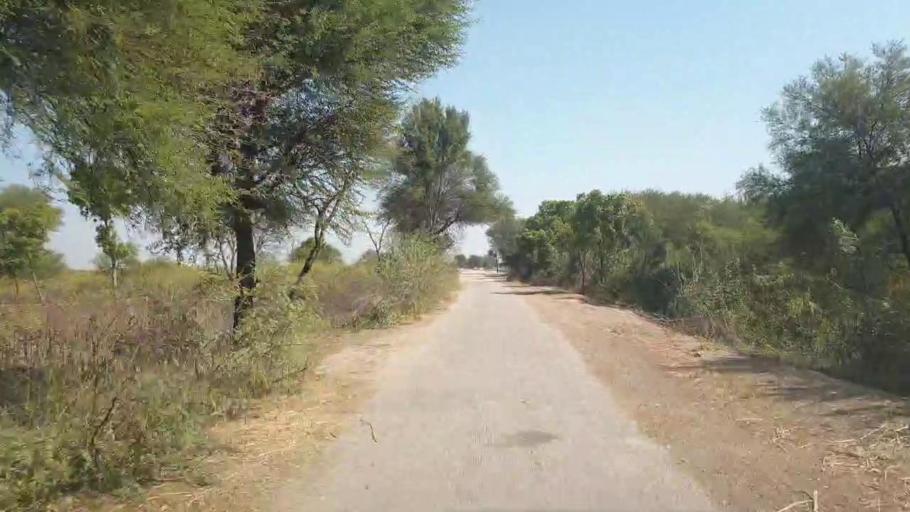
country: PK
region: Sindh
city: Chambar
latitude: 25.2887
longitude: 68.6878
